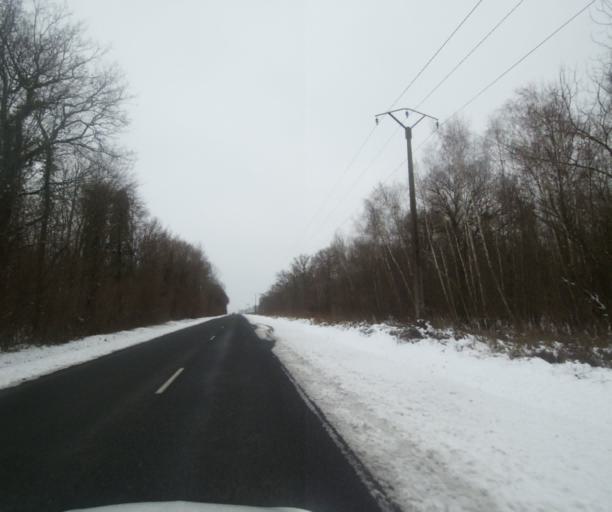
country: FR
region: Champagne-Ardenne
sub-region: Departement de la Haute-Marne
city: Villiers-en-Lieu
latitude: 48.6094
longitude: 4.8844
